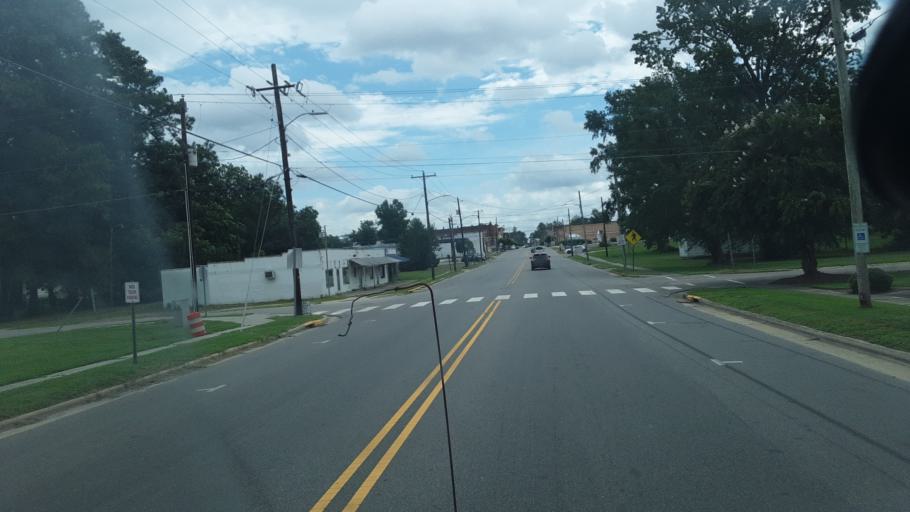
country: US
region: North Carolina
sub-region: Robeson County
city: Rowland
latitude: 34.5388
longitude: -79.2963
